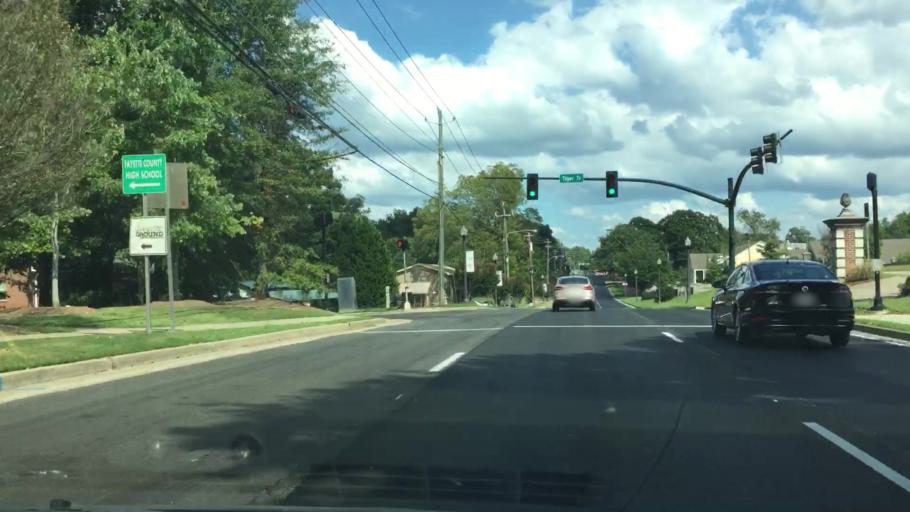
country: US
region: Georgia
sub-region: Fayette County
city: Fayetteville
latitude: 33.4478
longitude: -84.4610
